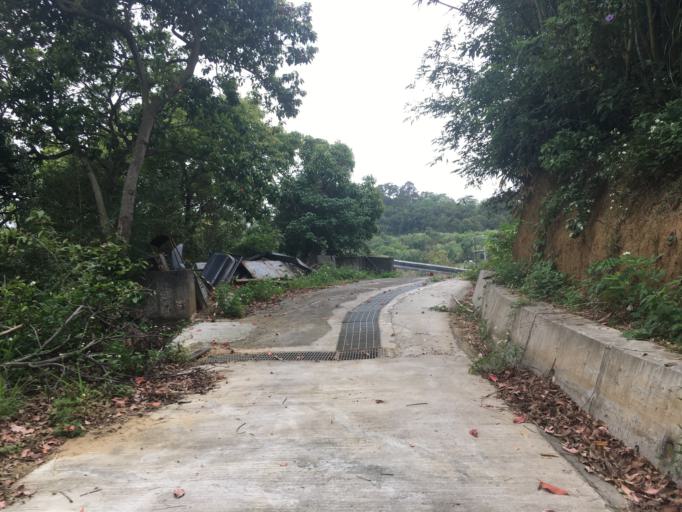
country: TW
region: Taiwan
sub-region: Hsinchu
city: Hsinchu
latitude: 24.7428
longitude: 120.9780
